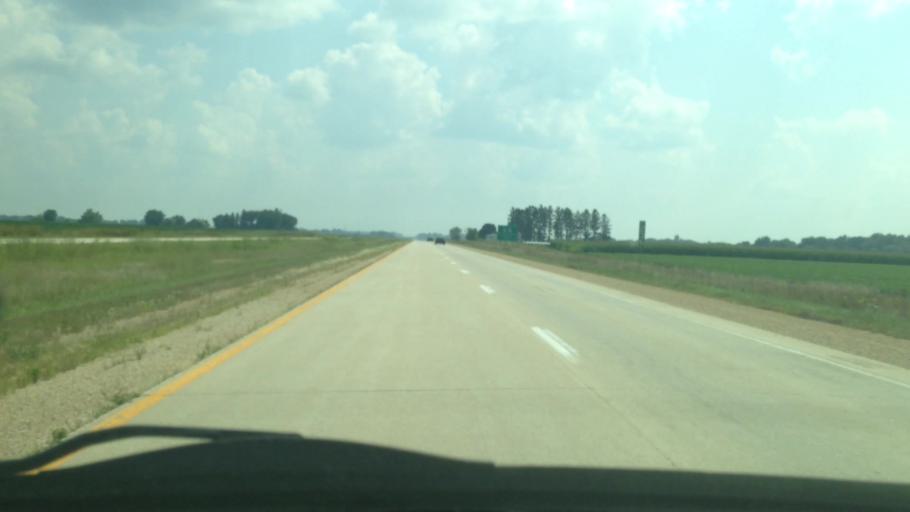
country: US
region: Iowa
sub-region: Chickasaw County
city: New Hampton
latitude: 42.9869
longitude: -92.3177
